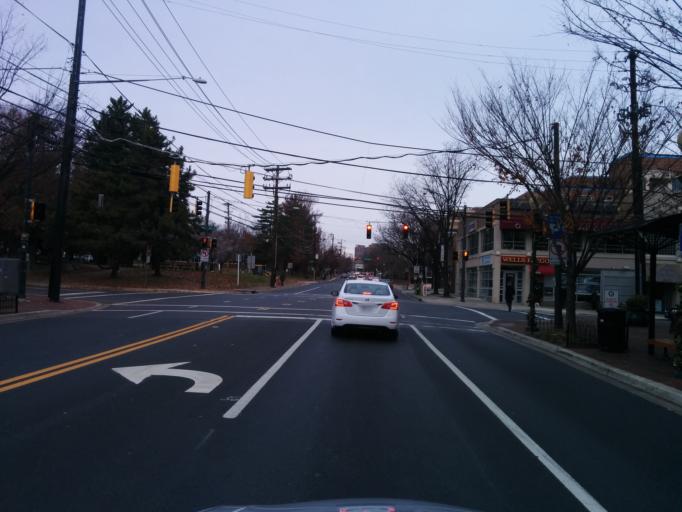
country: US
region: Maryland
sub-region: Montgomery County
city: Bethesda
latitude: 38.9818
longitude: -77.0984
